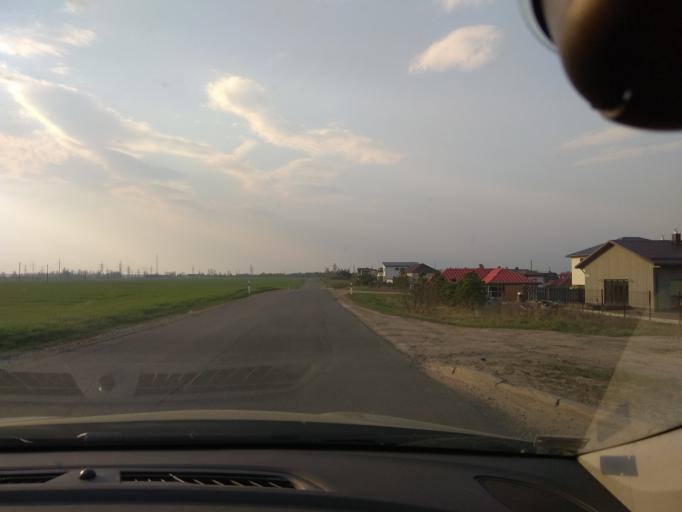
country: LT
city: Baltoji Voke
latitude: 54.6040
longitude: 25.1340
